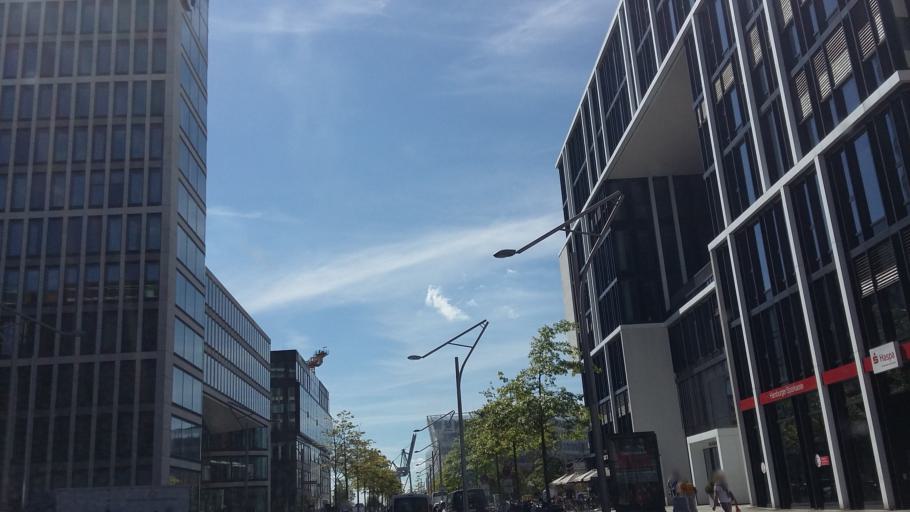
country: DE
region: Hamburg
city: Altstadt
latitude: 53.5418
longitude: 9.9934
